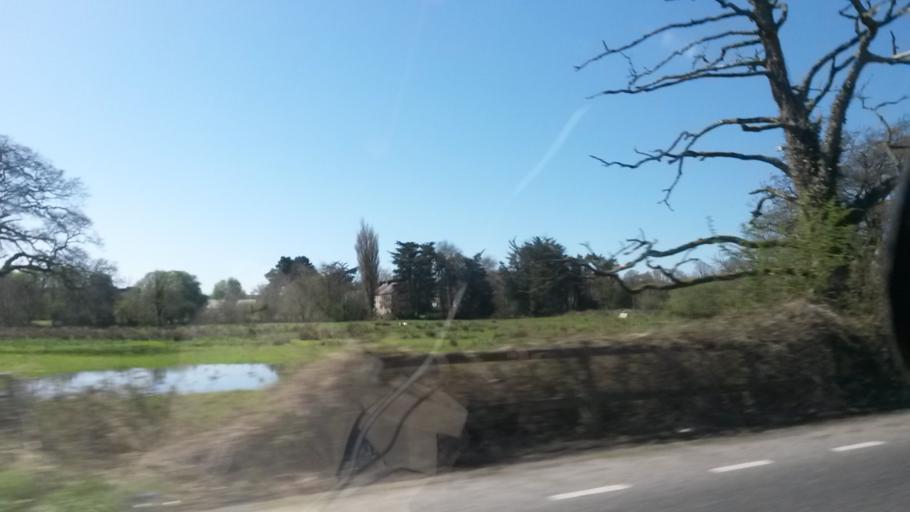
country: IE
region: Munster
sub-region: County Cork
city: Blarney
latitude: 51.8956
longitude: -8.5369
